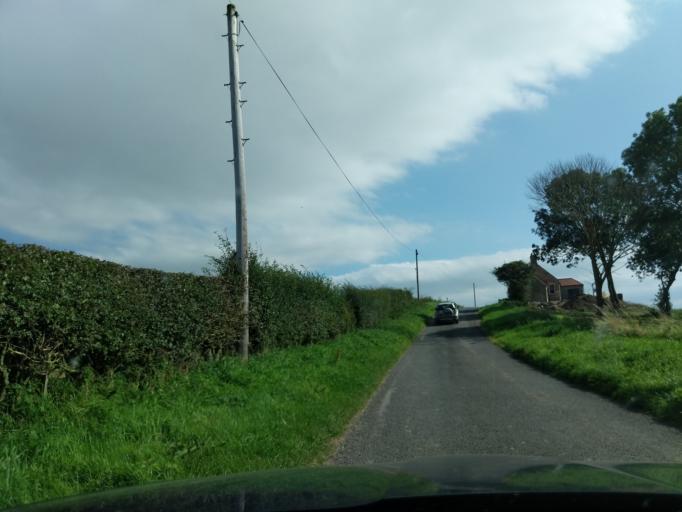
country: GB
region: England
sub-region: Northumberland
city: Ford
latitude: 55.6498
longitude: -2.1417
